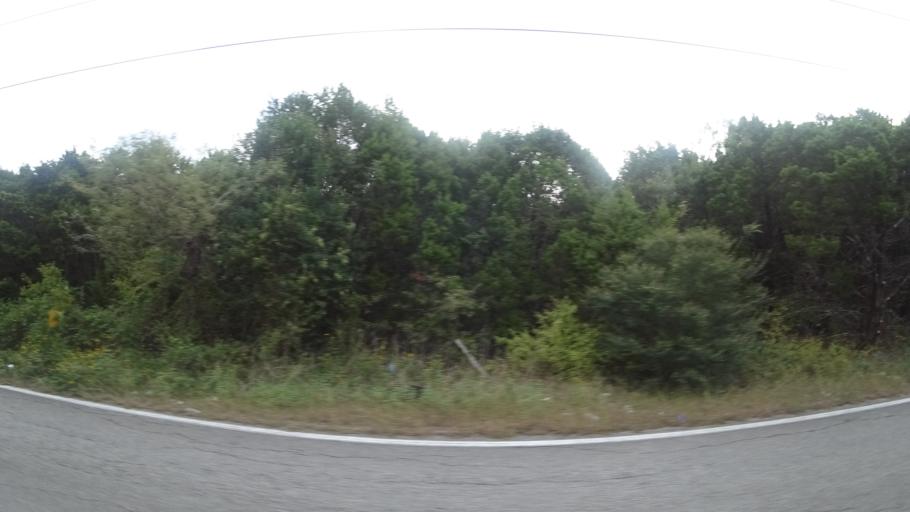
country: US
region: Texas
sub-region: Travis County
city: Pflugerville
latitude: 30.3639
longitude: -97.6503
